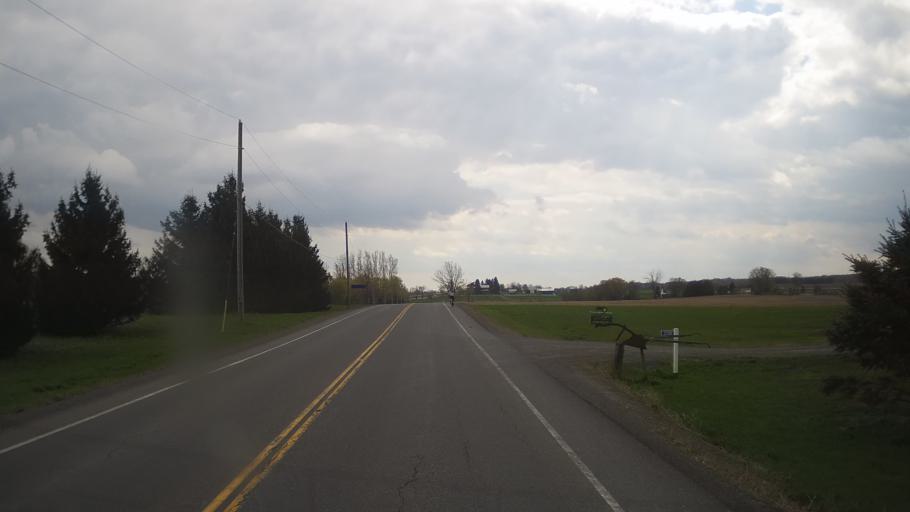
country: CA
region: Ontario
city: Hawkesbury
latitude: 45.5389
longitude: -74.5513
